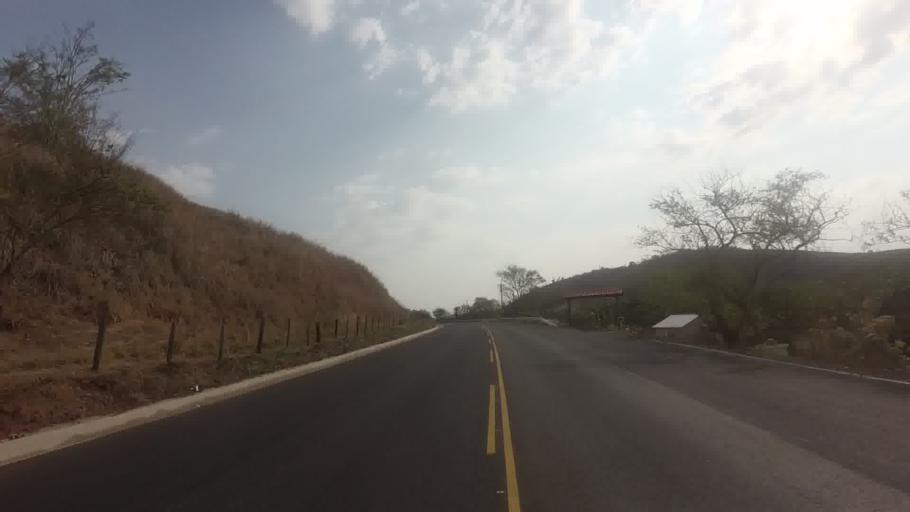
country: BR
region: Rio de Janeiro
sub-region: Itaperuna
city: Itaperuna
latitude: -21.3020
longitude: -41.8463
